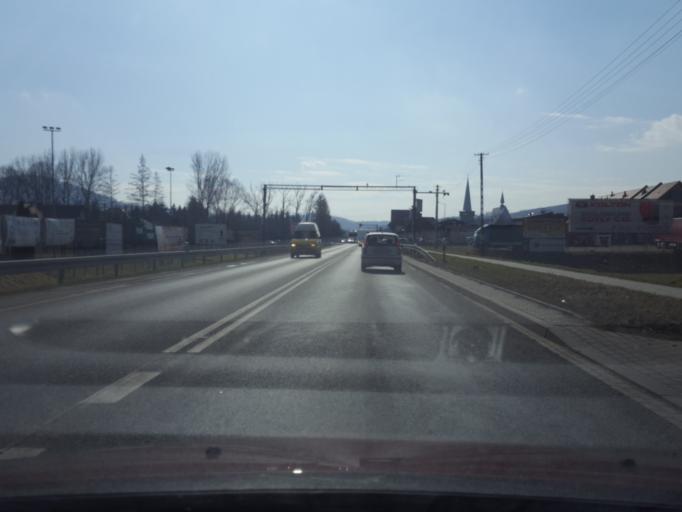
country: PL
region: Lesser Poland Voivodeship
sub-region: Powiat nowosadecki
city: Lososina Dolna
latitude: 49.7115
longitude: 20.6421
